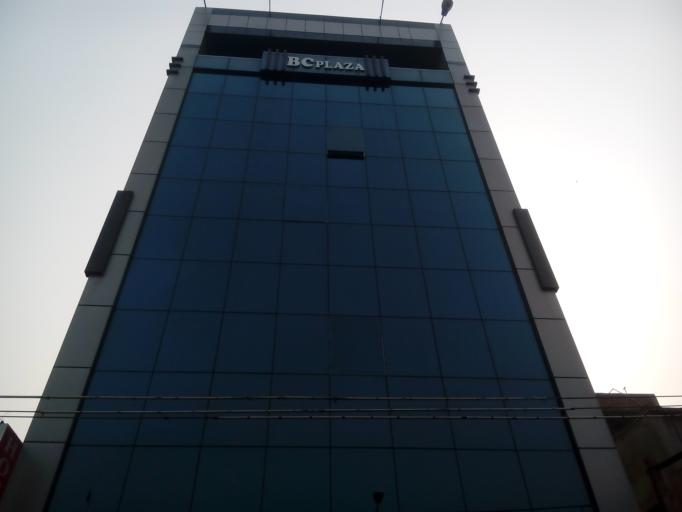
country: IN
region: Bihar
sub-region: Muzaffarpur
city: Muzaffarpur
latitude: 26.1201
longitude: 85.3845
